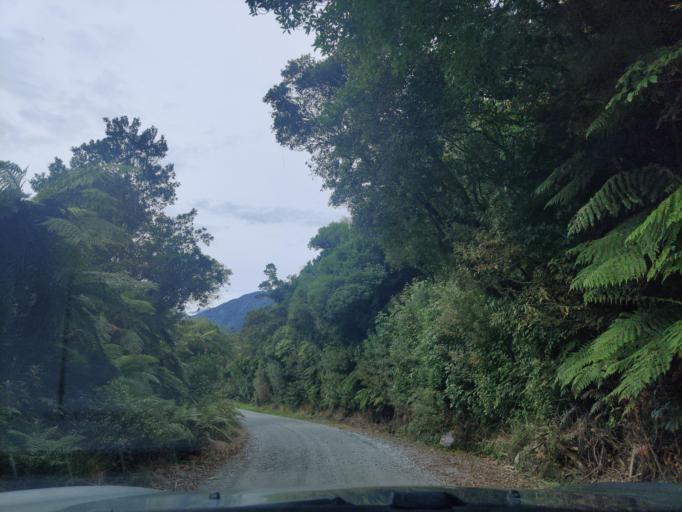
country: NZ
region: West Coast
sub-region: Westland District
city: Hokitika
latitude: -43.2917
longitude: 170.4055
